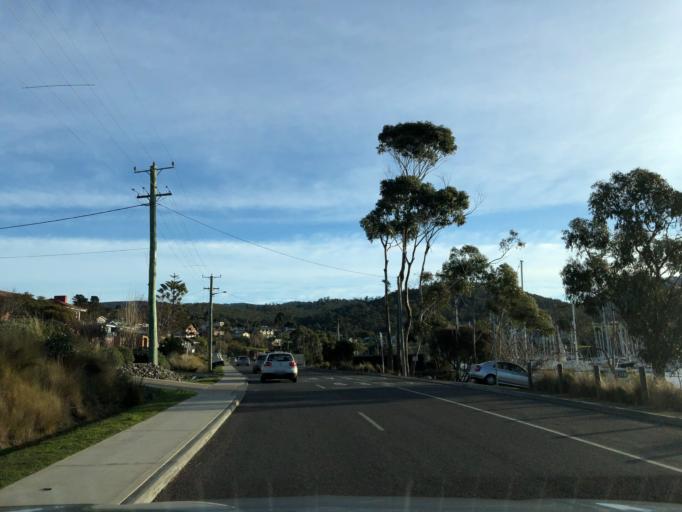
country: AU
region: Tasmania
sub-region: Kingborough
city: Kettering
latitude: -43.1276
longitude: 147.2539
